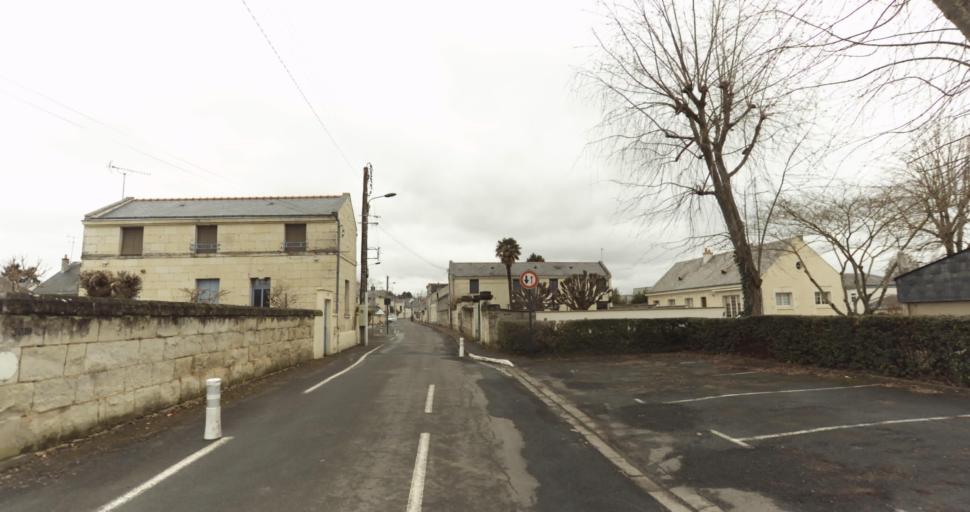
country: FR
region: Pays de la Loire
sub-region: Departement de Maine-et-Loire
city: Distre
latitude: 47.2409
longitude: -0.0936
